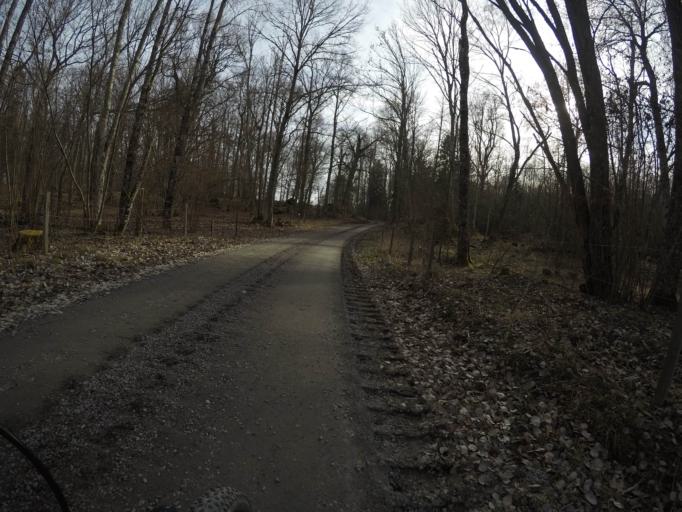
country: SE
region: Soedermanland
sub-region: Eskilstuna Kommun
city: Hallbybrunn
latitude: 59.4471
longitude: 16.3938
